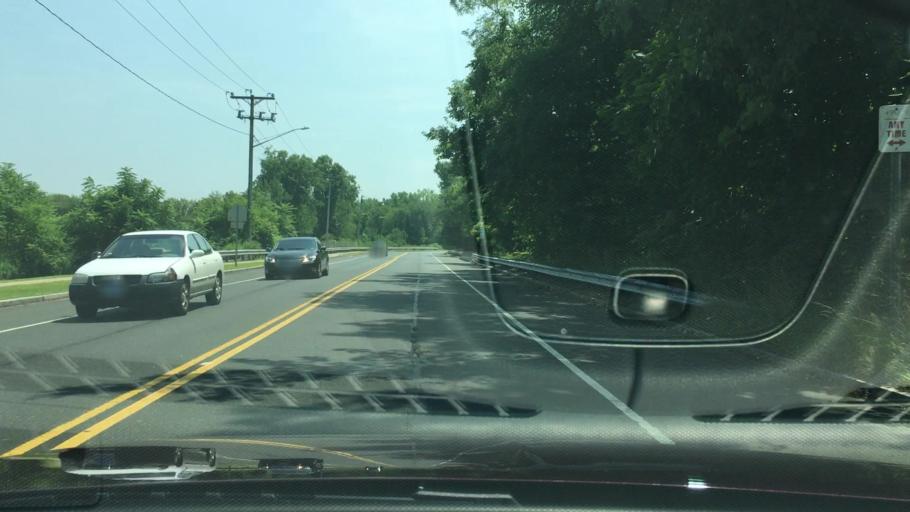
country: US
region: Connecticut
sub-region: Hartford County
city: East Hartford
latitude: 41.7770
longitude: -72.6060
